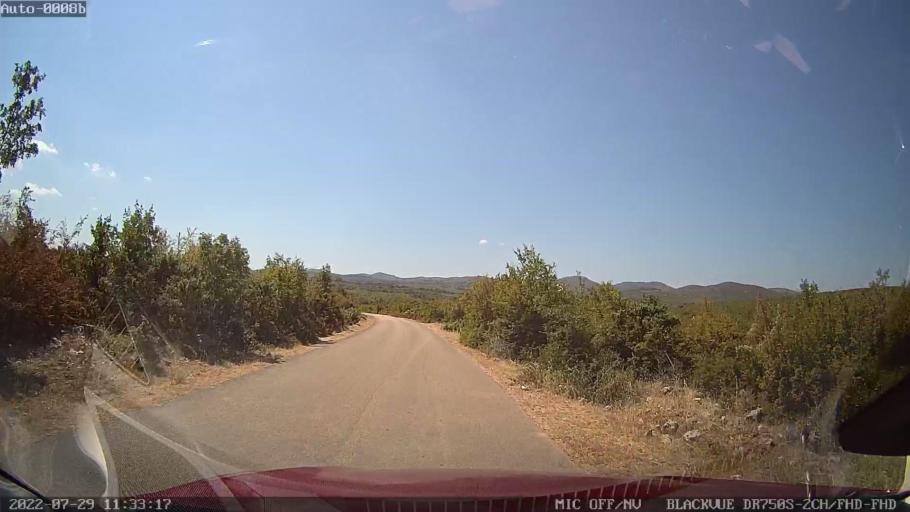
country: HR
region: Zadarska
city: Obrovac
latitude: 44.1874
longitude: 15.7328
